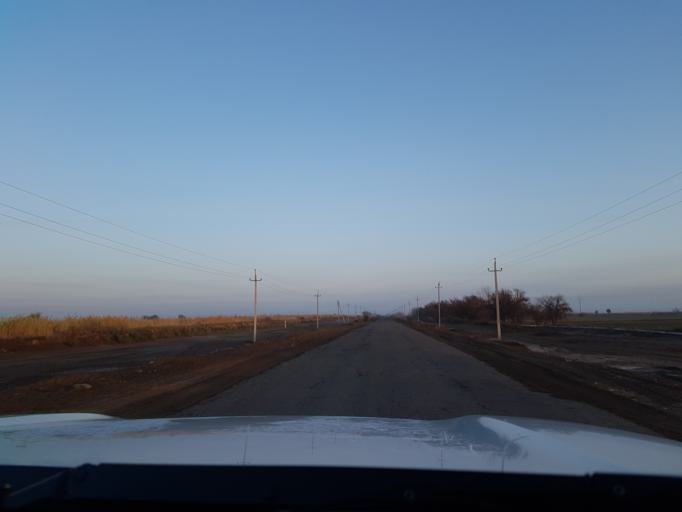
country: TM
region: Dasoguz
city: Koeneuergench
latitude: 41.8359
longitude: 58.7042
